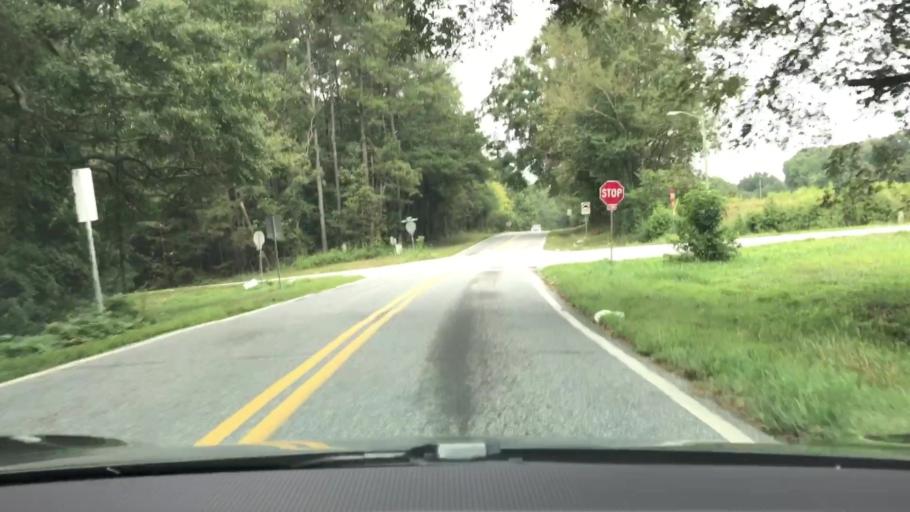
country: US
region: Georgia
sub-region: Barrow County
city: Auburn
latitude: 34.0325
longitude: -83.7958
